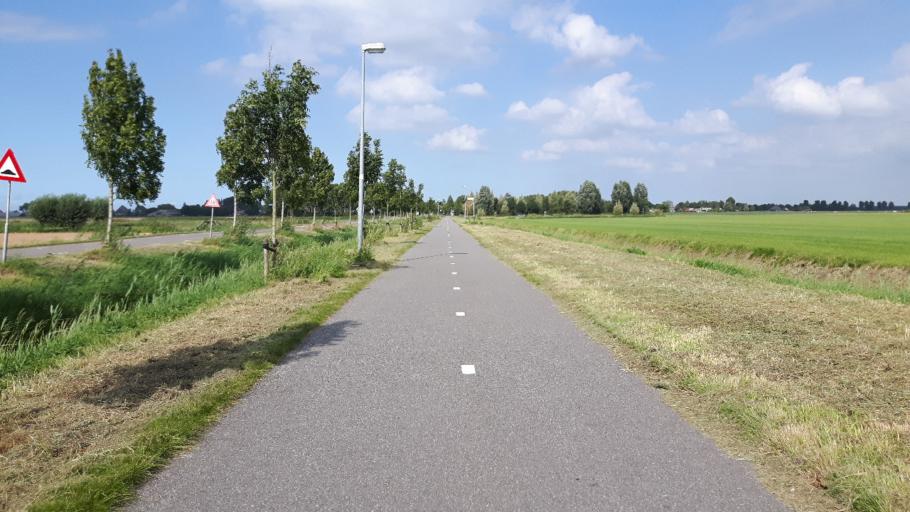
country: NL
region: North Holland
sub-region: Gemeente Medemblik
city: Opperdoes
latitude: 52.7169
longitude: 5.0917
